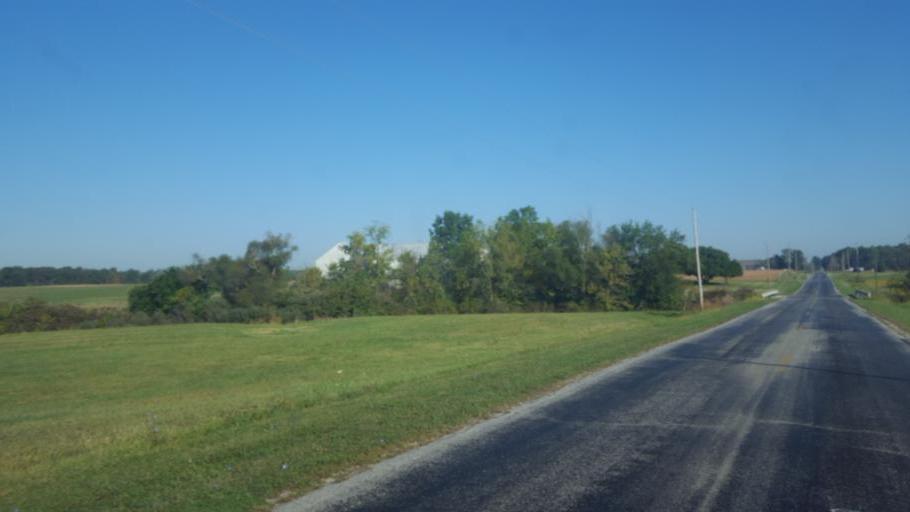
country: US
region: Ohio
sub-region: Union County
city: Richwood
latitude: 40.5296
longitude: -83.3865
